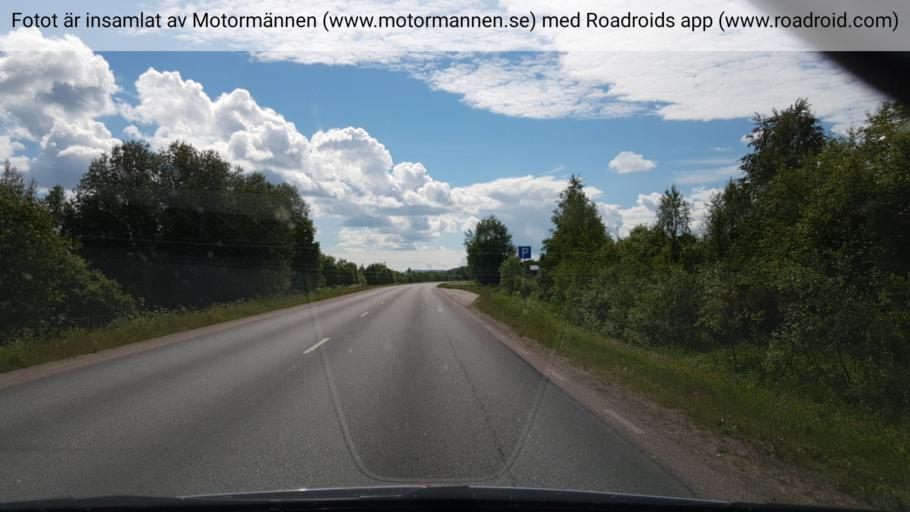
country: SE
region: Norrbotten
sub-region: Overtornea Kommun
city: OEvertornea
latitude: 66.4283
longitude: 23.6268
